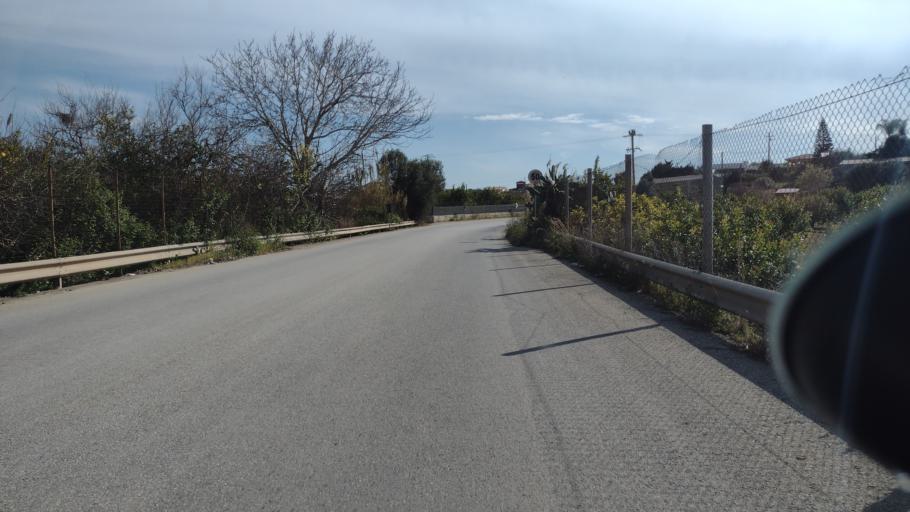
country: IT
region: Sicily
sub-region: Provincia di Siracusa
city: Avola
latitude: 36.8756
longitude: 15.1271
